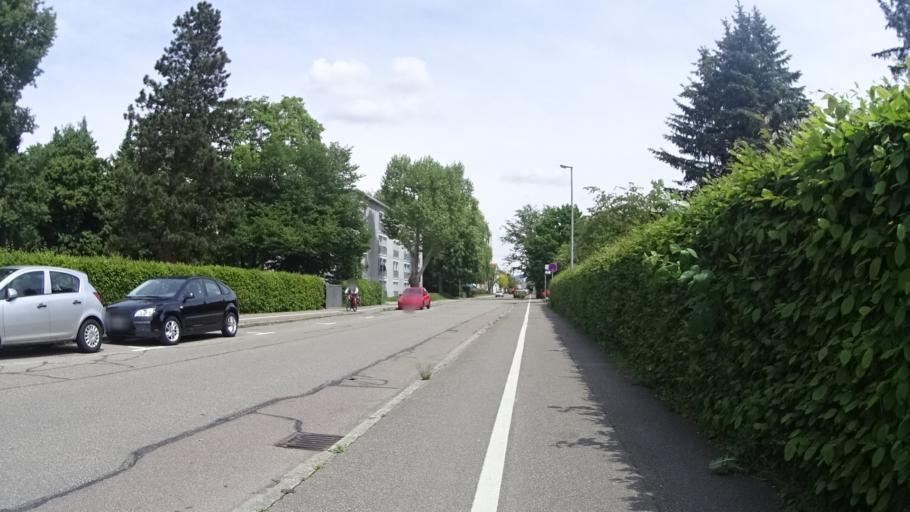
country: DE
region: Baden-Wuerttemberg
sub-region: Freiburg Region
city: Rheinfelden (Baden)
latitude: 47.5580
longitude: 7.7774
